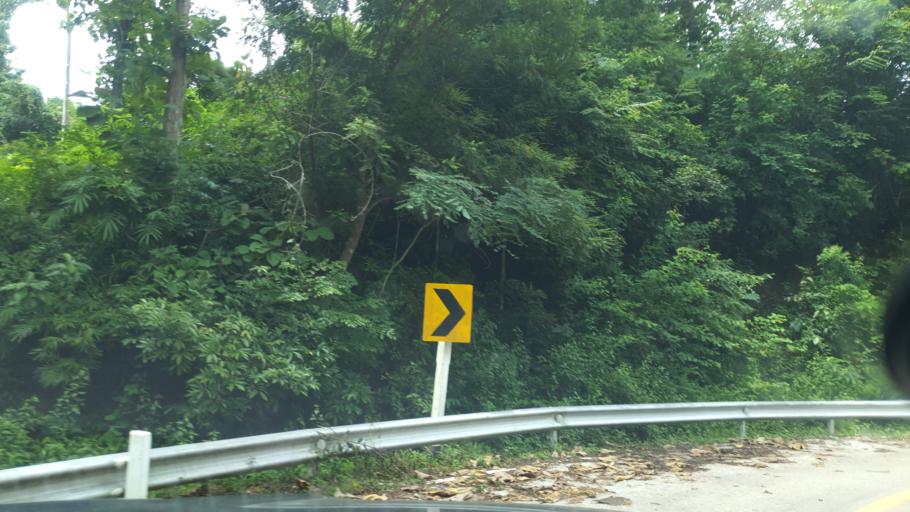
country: TH
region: Lampang
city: Hang Chat
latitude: 18.3642
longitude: 99.2601
